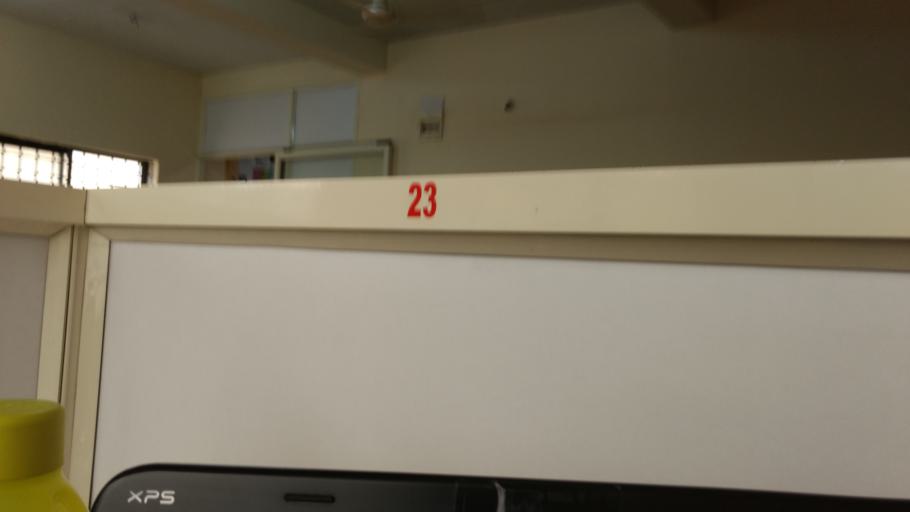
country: IN
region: Karnataka
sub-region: Bangalore Urban
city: Bangalore
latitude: 13.0221
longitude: 77.6393
